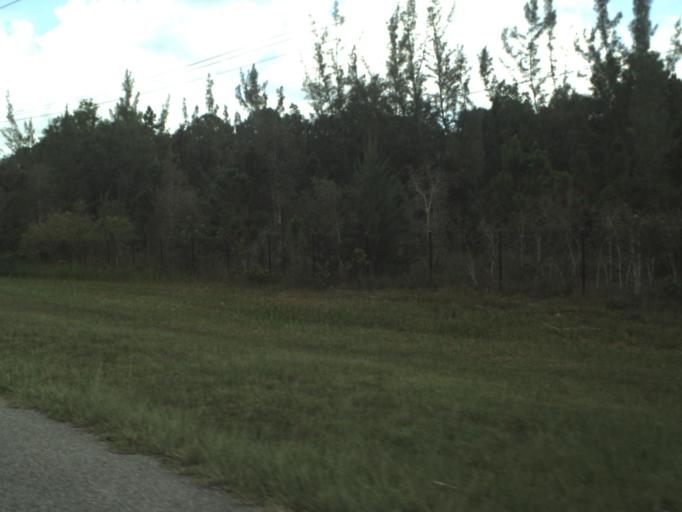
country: US
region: Florida
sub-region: Palm Beach County
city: Limestone Creek
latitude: 26.8911
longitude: -80.2736
